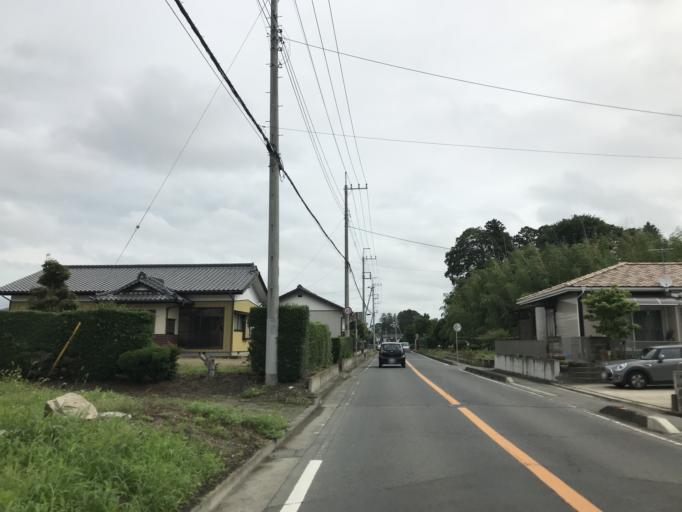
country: JP
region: Ibaraki
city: Mito-shi
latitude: 36.3309
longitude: 140.4563
